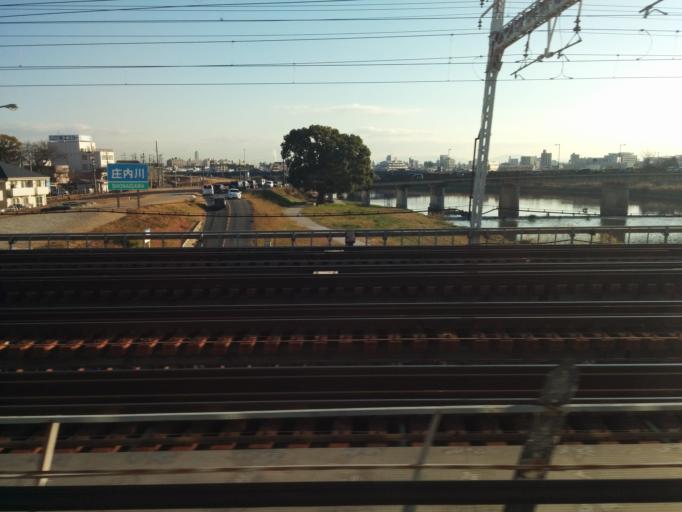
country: JP
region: Aichi
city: Nagoya-shi
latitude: 35.1926
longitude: 136.8653
